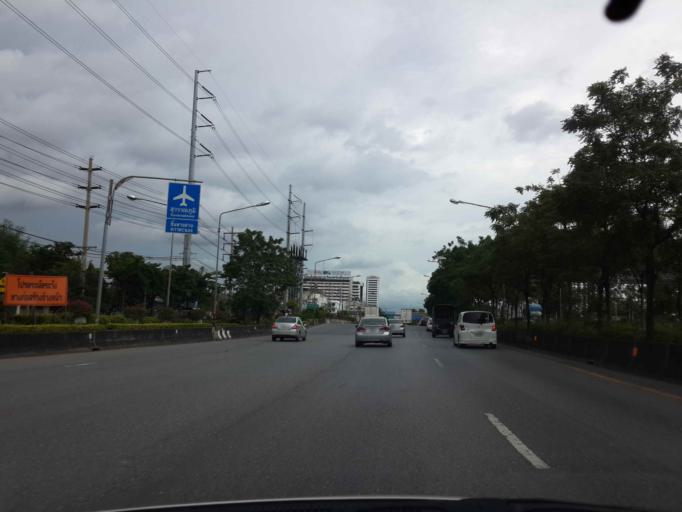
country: TH
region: Bangkok
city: Chom Thong
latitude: 13.6798
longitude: 100.4694
